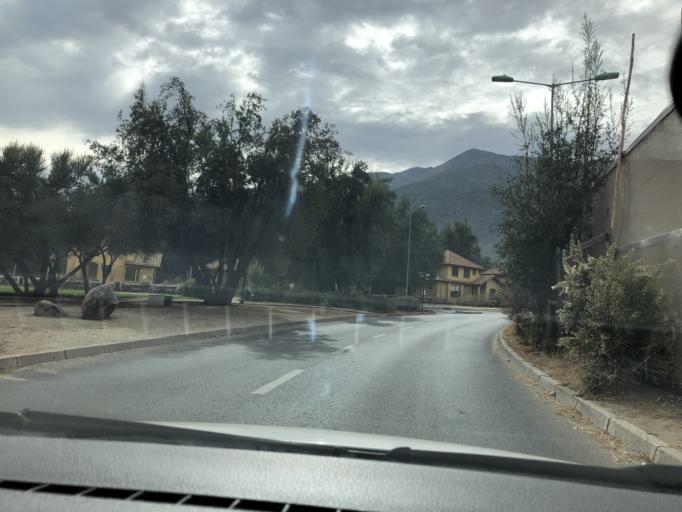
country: CL
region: Santiago Metropolitan
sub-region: Provincia de Cordillera
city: Puente Alto
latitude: -33.5879
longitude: -70.5095
